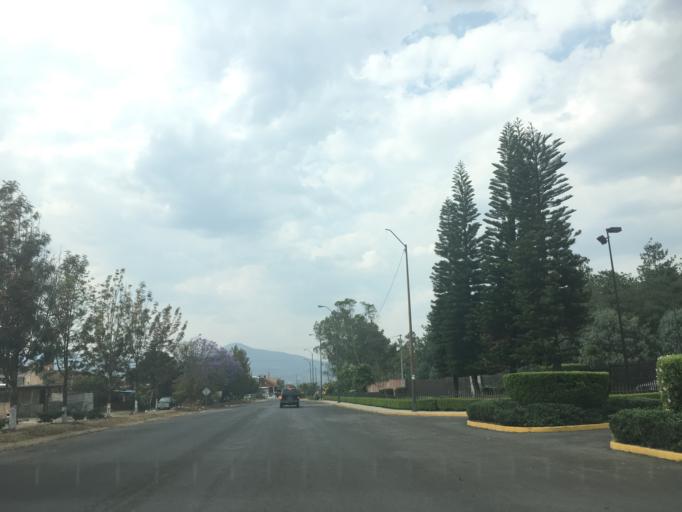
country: MX
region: Michoacan
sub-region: Morelia
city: Morelos
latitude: 19.6506
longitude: -101.2309
